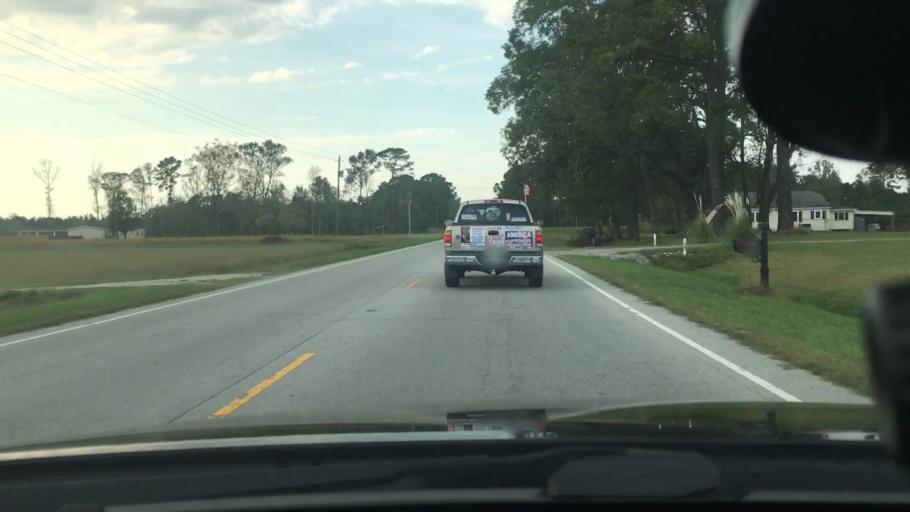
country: US
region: North Carolina
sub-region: Craven County
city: Vanceboro
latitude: 35.2720
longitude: -77.1132
